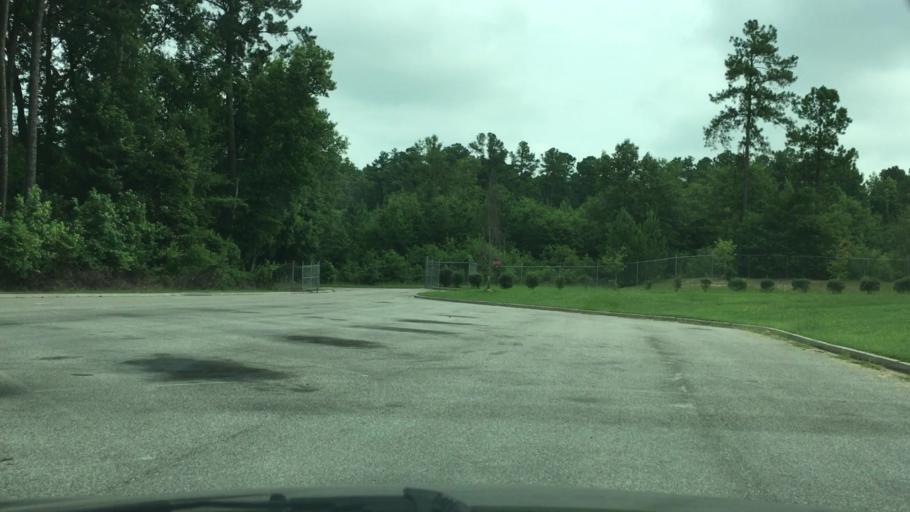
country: US
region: South Carolina
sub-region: Aiken County
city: Belvedere
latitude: 33.5418
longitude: -81.9572
